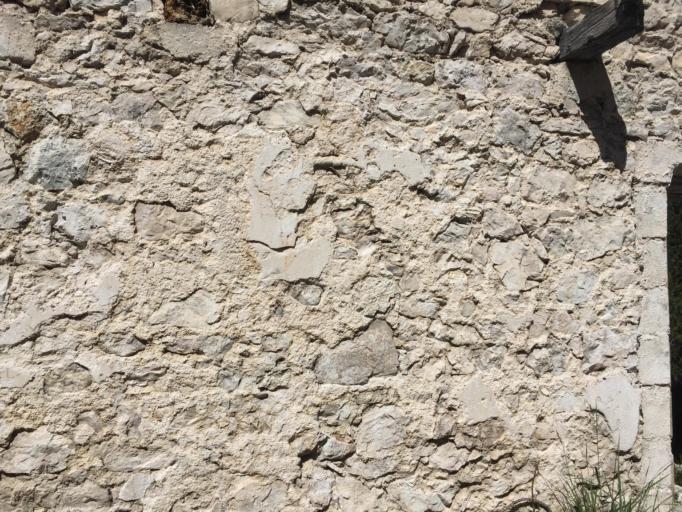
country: IT
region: Friuli Venezia Giulia
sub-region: Provincia di Udine
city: Dogna
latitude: 46.4391
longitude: 13.2674
